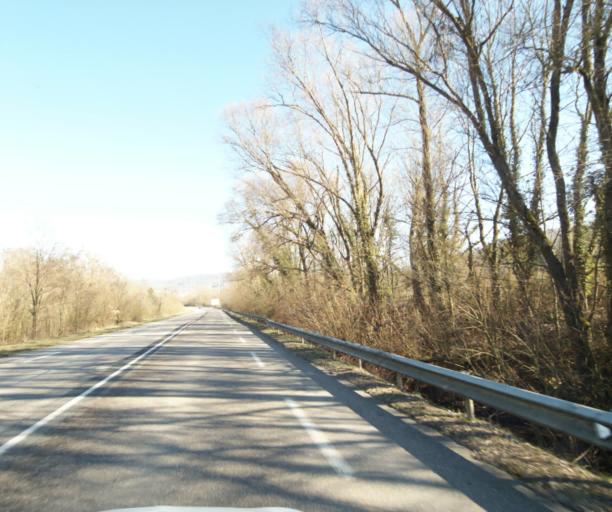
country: FR
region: Lorraine
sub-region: Departement de Meurthe-et-Moselle
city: Lay-Saint-Christophe
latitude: 48.7370
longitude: 6.1831
